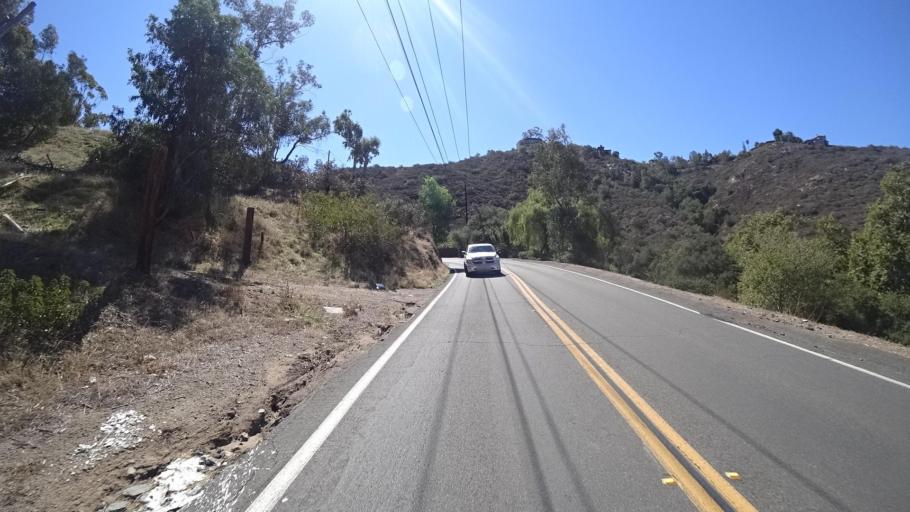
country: US
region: California
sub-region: San Diego County
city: Jamul
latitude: 32.7312
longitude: -116.8782
